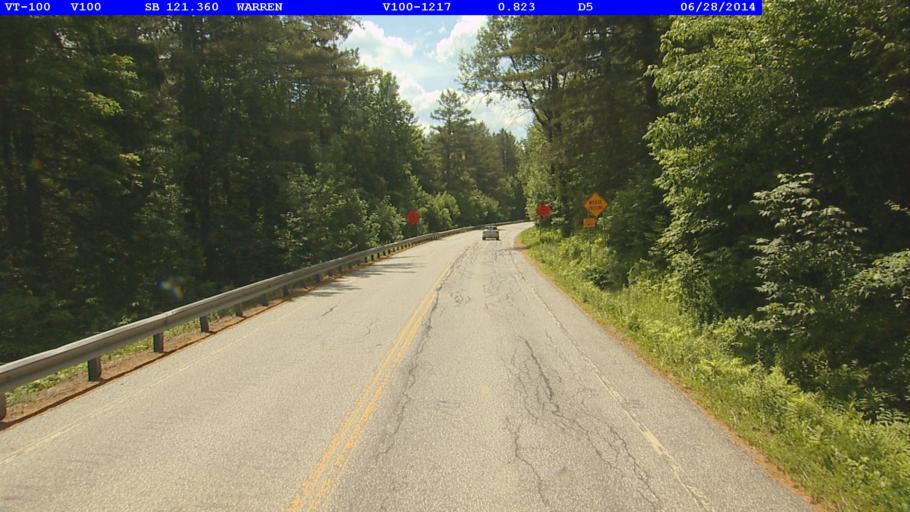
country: US
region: Vermont
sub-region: Washington County
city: Northfield
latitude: 44.0714
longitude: -72.8597
